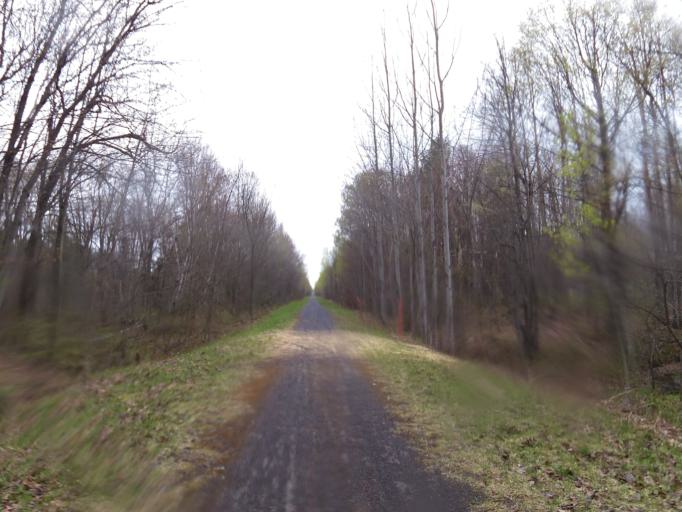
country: CA
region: Ontario
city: Bourget
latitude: 45.4319
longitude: -75.2689
